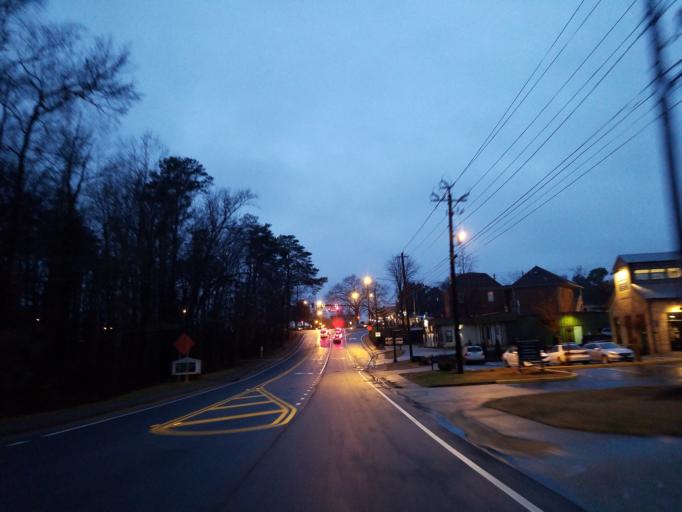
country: US
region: Georgia
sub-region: Fulton County
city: Roswell
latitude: 34.0254
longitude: -84.3586
